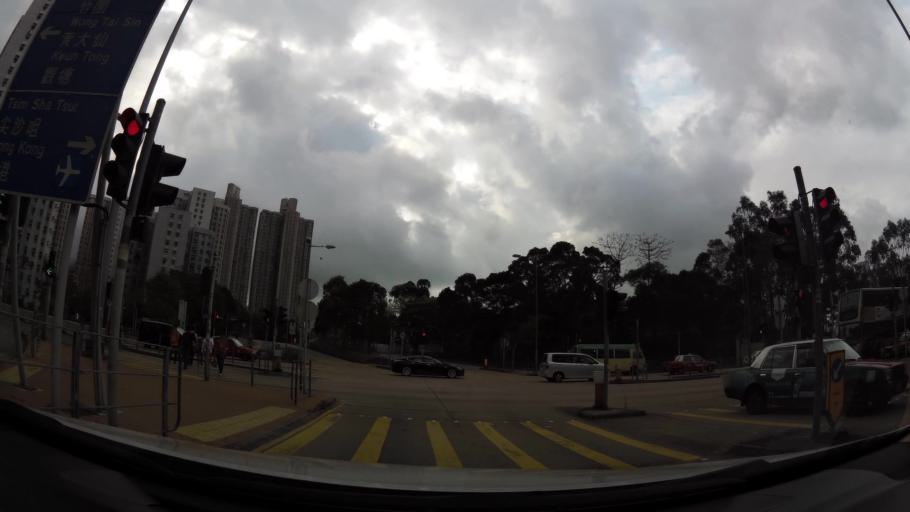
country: HK
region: Wong Tai Sin
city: Wong Tai Sin
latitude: 22.3399
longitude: 114.1830
